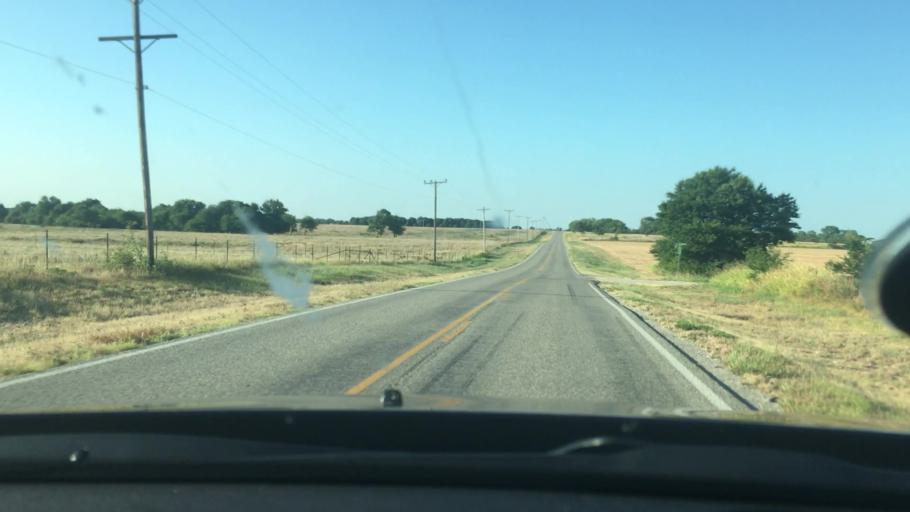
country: US
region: Oklahoma
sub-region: Murray County
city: Sulphur
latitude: 34.5794
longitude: -96.8448
